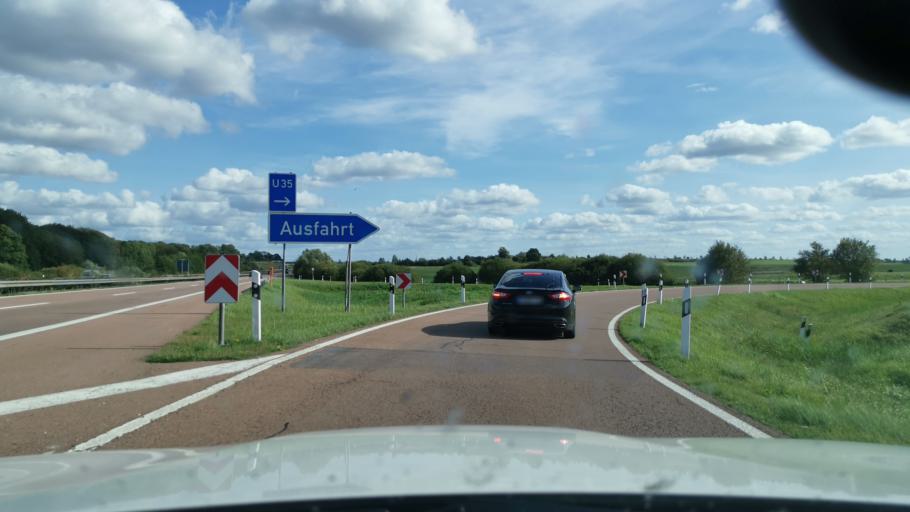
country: DE
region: Mecklenburg-Vorpommern
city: Tessin
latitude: 54.0305
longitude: 12.4102
